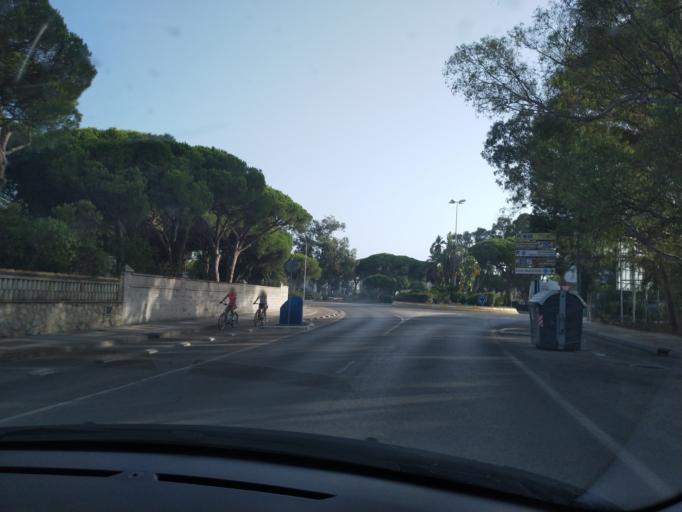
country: ES
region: Andalusia
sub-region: Provincia de Cadiz
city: Chiclana de la Frontera
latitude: 36.3811
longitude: -6.1913
